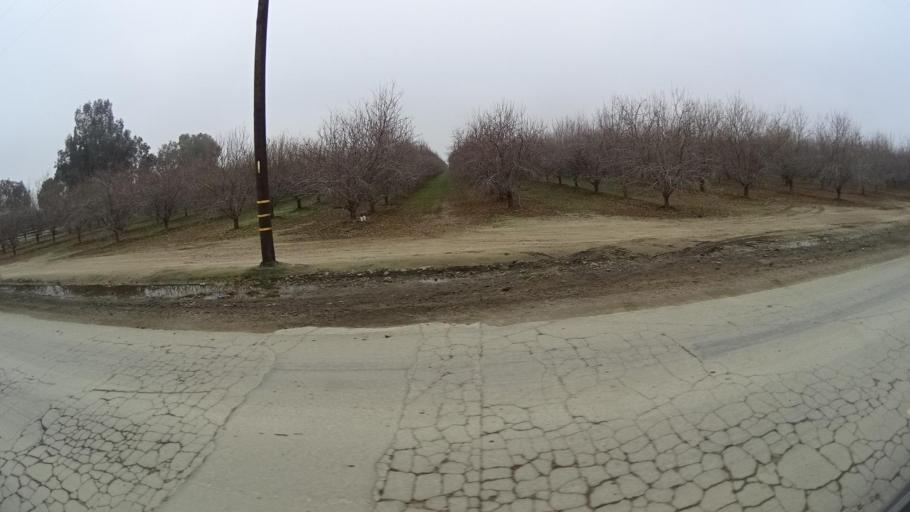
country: US
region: California
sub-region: Kern County
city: Greenfield
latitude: 35.2379
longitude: -119.0441
